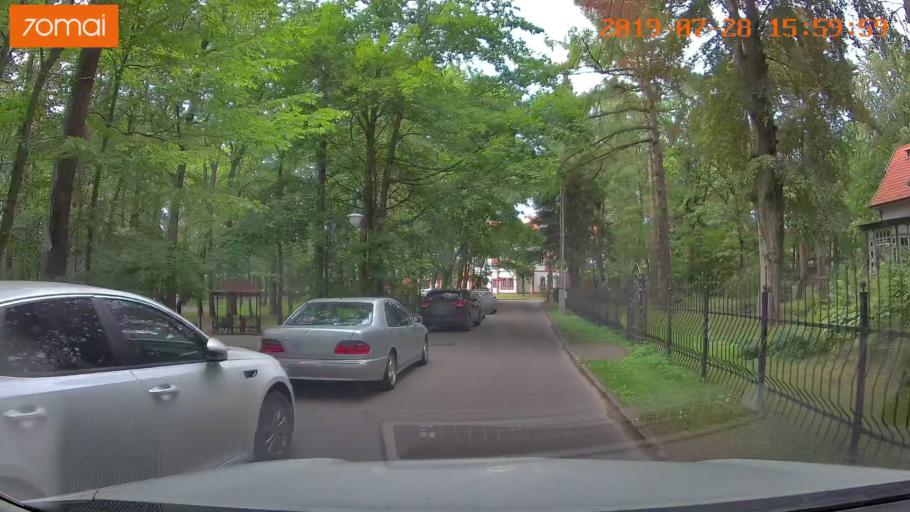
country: RU
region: Kaliningrad
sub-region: Gorod Svetlogorsk
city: Svetlogorsk
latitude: 54.9427
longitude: 20.1572
